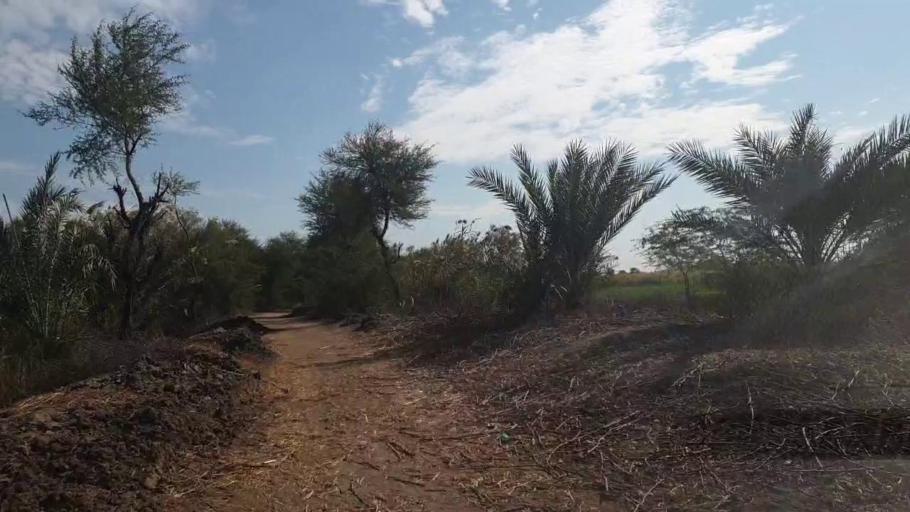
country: PK
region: Sindh
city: Jhol
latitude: 26.0092
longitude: 68.8790
